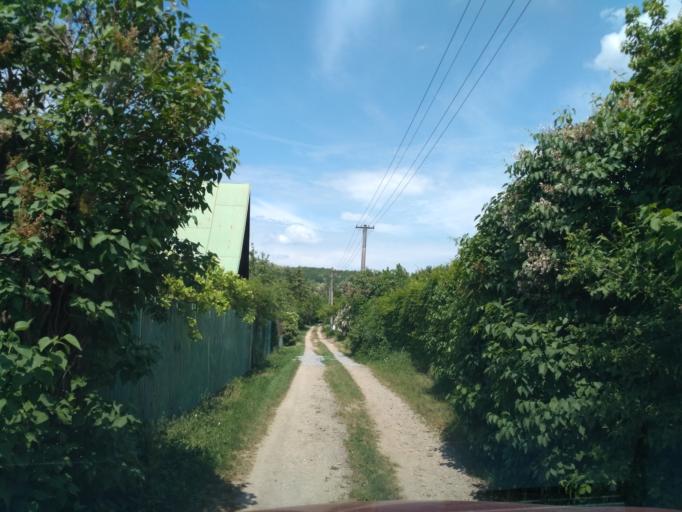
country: SK
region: Kosicky
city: Kosice
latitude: 48.7286
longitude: 21.2238
